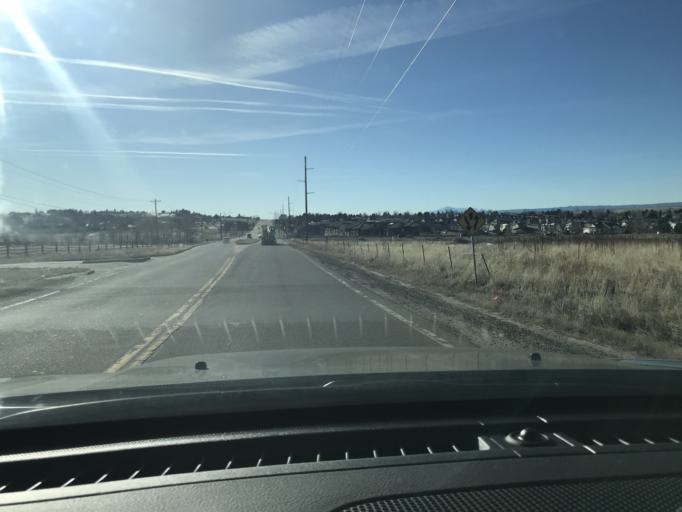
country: US
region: Colorado
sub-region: Douglas County
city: Parker
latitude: 39.5389
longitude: -104.7559
